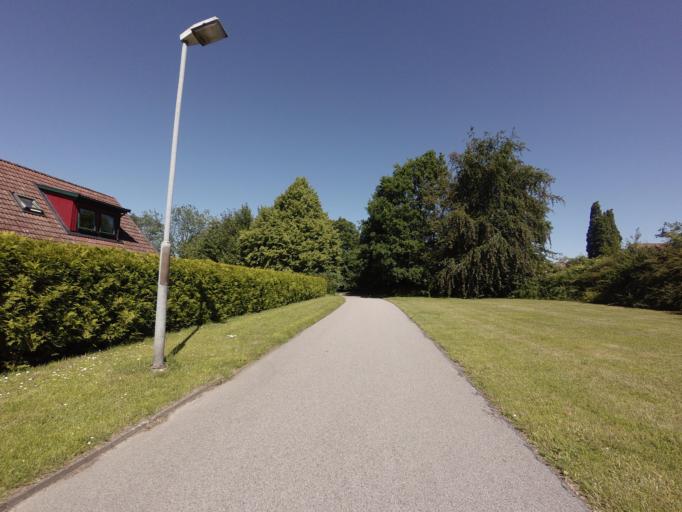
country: SE
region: Skane
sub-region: Vellinge Kommun
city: Hollviken
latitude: 55.4136
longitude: 12.9815
